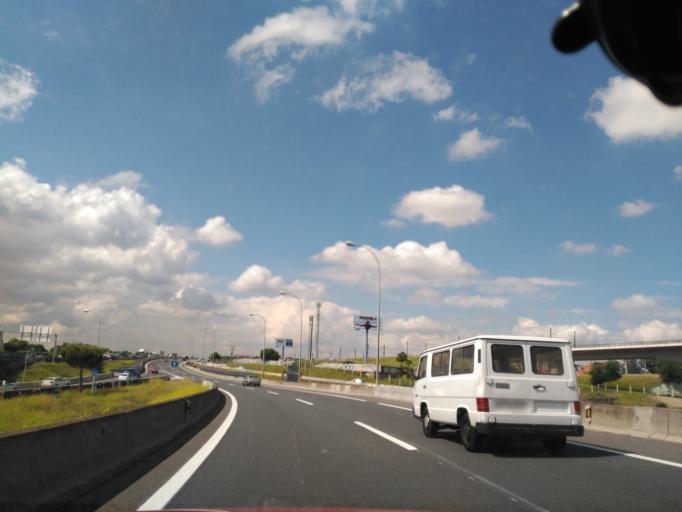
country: ES
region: Madrid
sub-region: Provincia de Madrid
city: Villaverde
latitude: 40.3608
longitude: -3.6776
